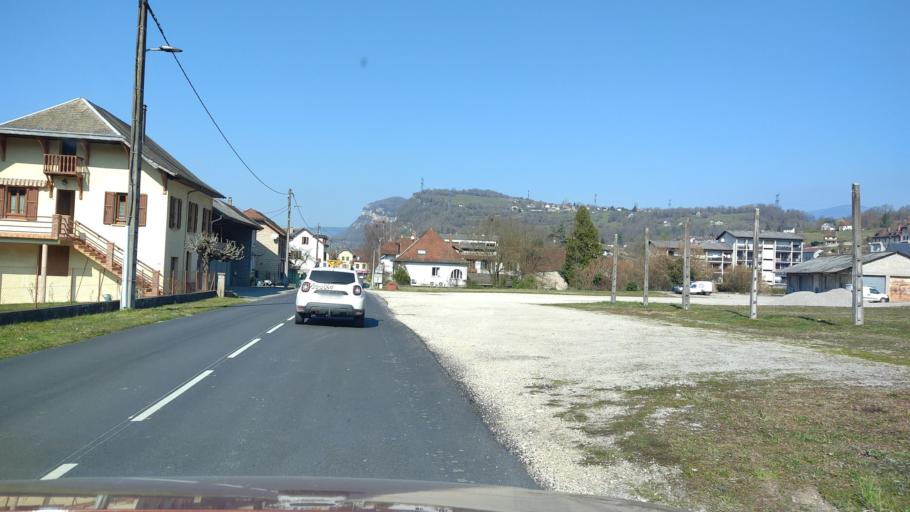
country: FR
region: Rhone-Alpes
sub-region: Departement de la Savoie
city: La Bridoire
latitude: 45.5230
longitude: 5.7392
